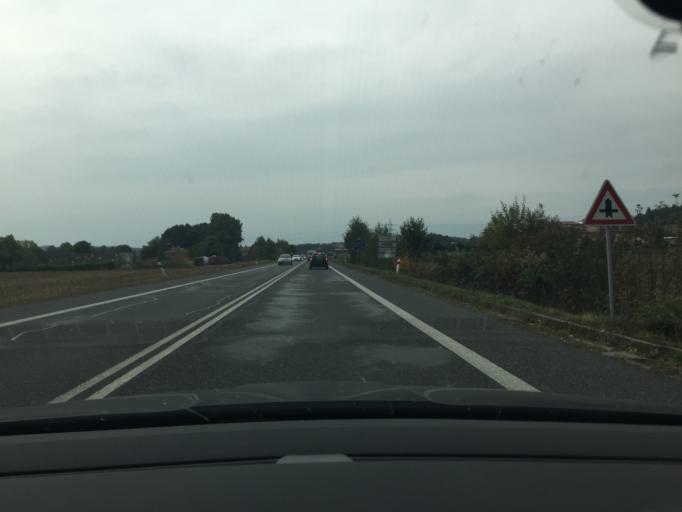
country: CZ
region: Central Bohemia
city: Milin
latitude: 49.6537
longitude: 14.0575
